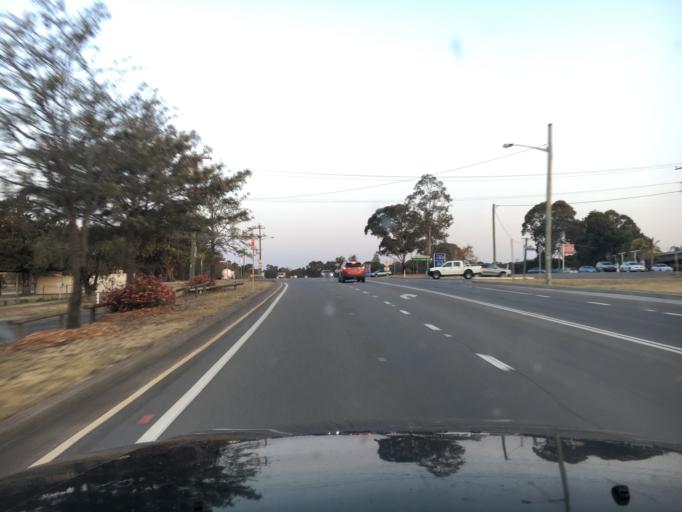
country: AU
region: New South Wales
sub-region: Cessnock
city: Greta
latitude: -32.6818
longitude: 151.3926
